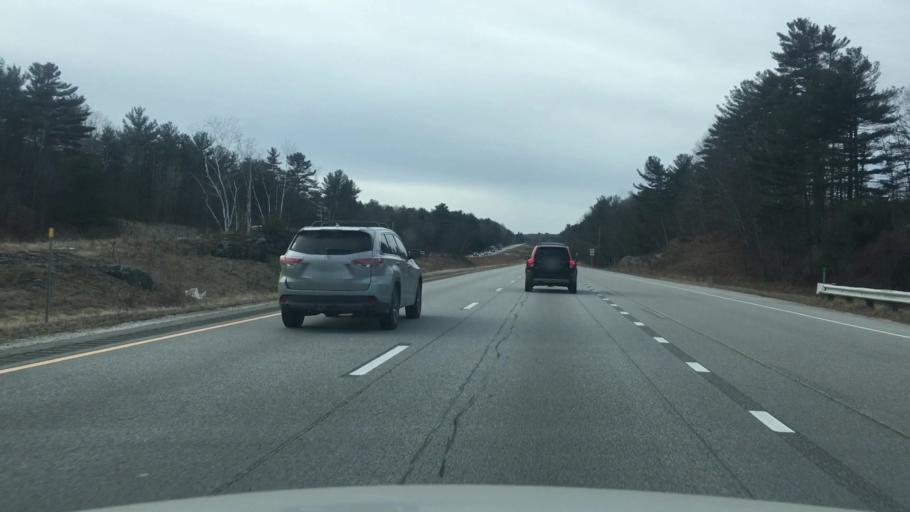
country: US
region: New Hampshire
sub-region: Rockingham County
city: Raymond
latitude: 43.0237
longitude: -71.2018
